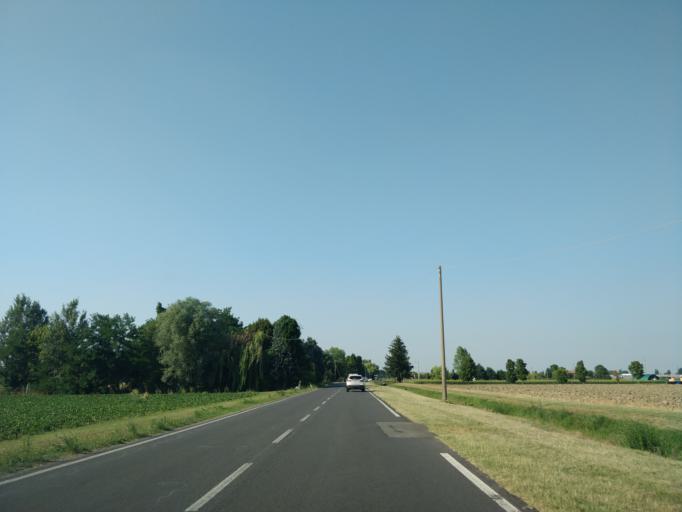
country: IT
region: Emilia-Romagna
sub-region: Provincia di Bologna
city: Argelato
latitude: 44.6263
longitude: 11.3388
